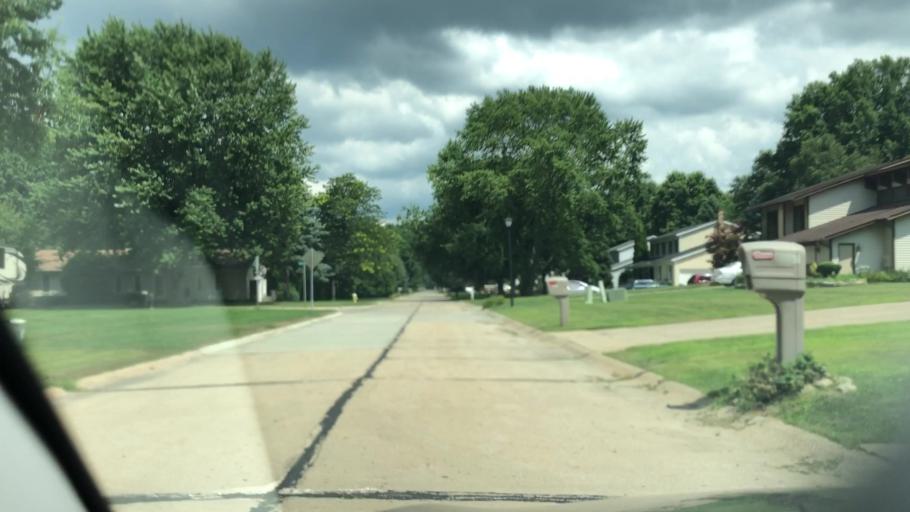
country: US
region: Ohio
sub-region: Summit County
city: Fairlawn
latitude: 41.1217
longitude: -81.6339
